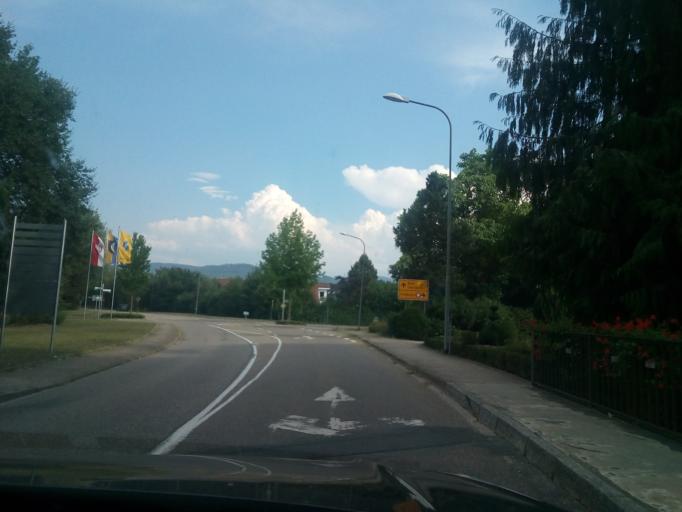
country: DE
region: Baden-Wuerttemberg
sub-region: Karlsruhe Region
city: Ottenhofen
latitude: 48.7384
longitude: 8.1302
